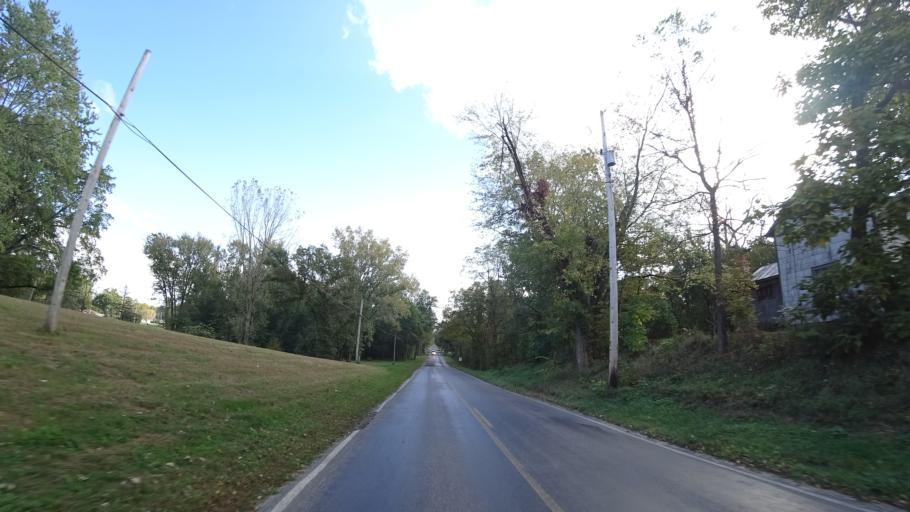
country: US
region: Michigan
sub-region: Saint Joseph County
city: Centreville
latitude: 41.9320
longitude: -85.5282
